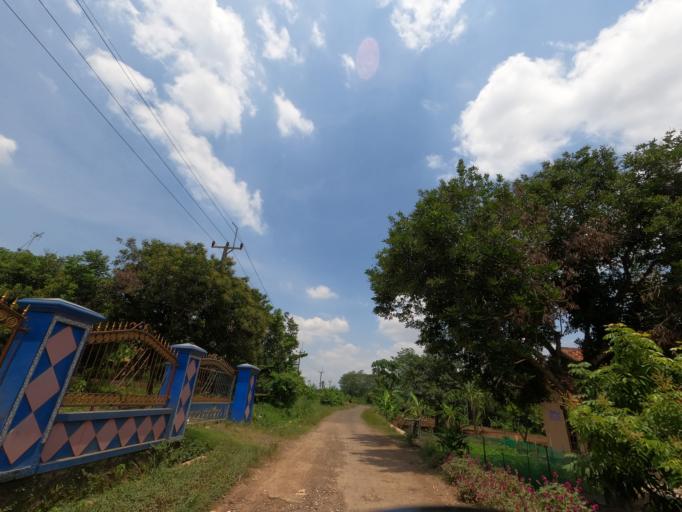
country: ID
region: West Java
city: Pamanukan
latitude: -6.5098
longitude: 107.7701
